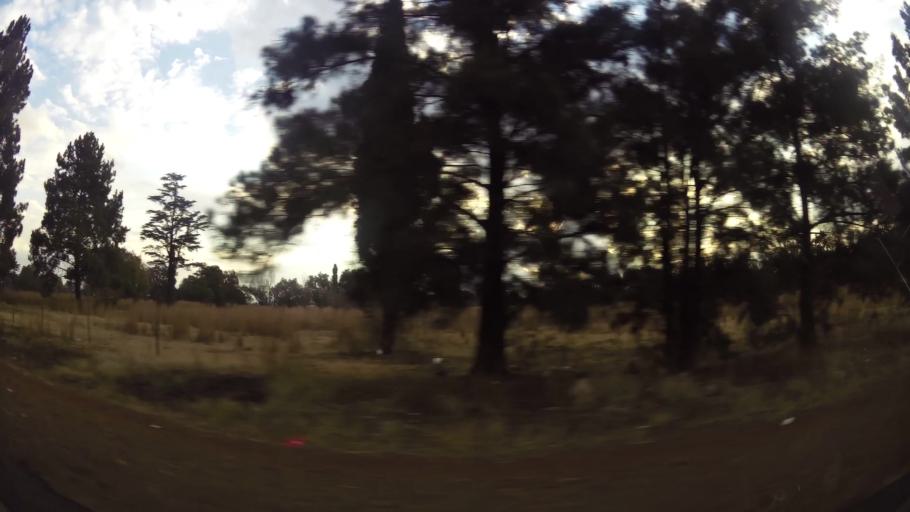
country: ZA
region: Gauteng
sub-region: Sedibeng District Municipality
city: Vanderbijlpark
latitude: -26.6367
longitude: 27.8070
